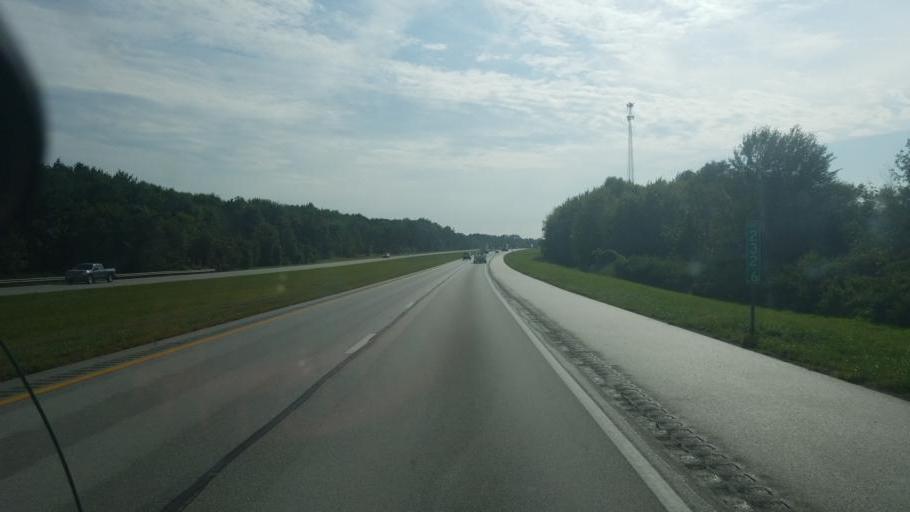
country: US
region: Ohio
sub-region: Ashtabula County
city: North Kingsville
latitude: 41.8512
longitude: -80.7014
